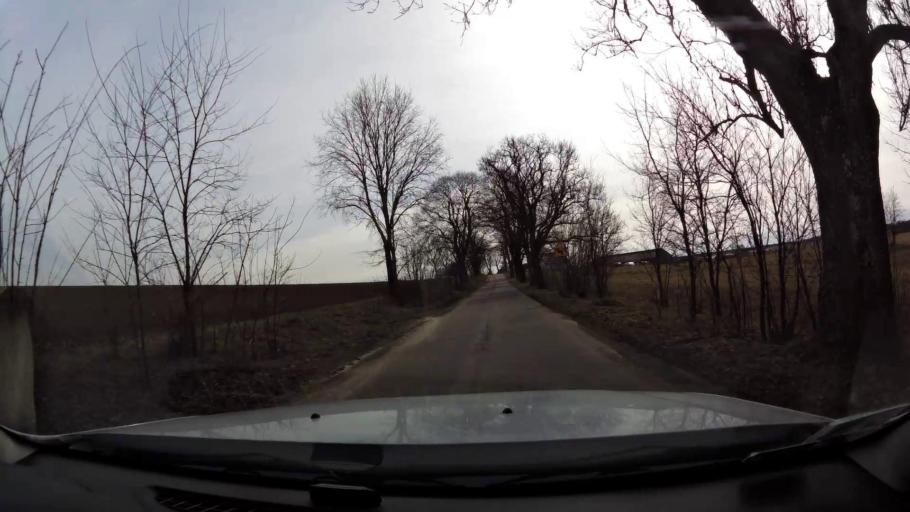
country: PL
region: West Pomeranian Voivodeship
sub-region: Powiat stargardzki
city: Insko
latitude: 53.4590
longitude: 15.6095
